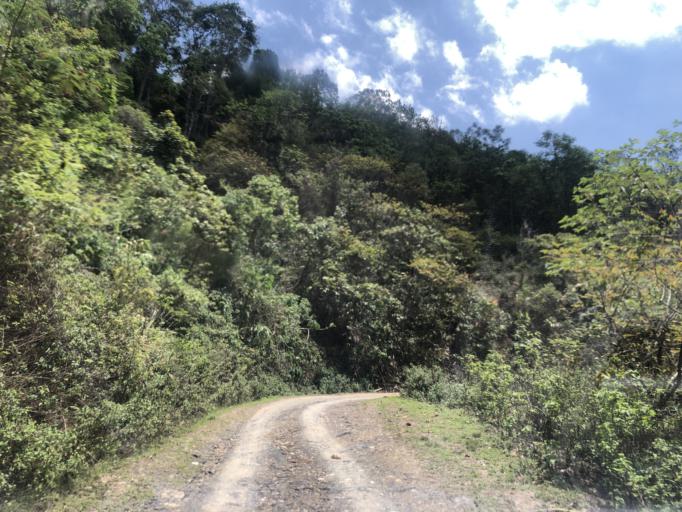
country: LA
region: Phongsali
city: Phongsali
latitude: 21.4444
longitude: 102.1637
